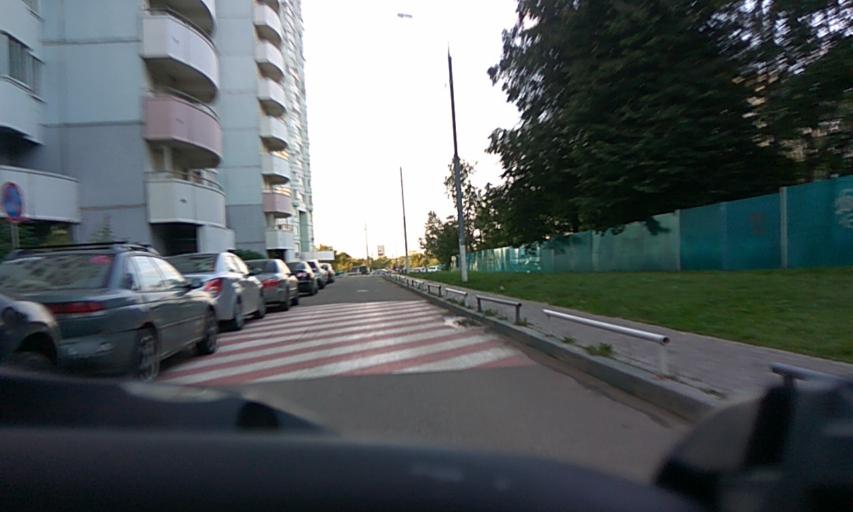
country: RU
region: Moskovskaya
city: Kozhukhovo
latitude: 55.6853
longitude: 37.6773
